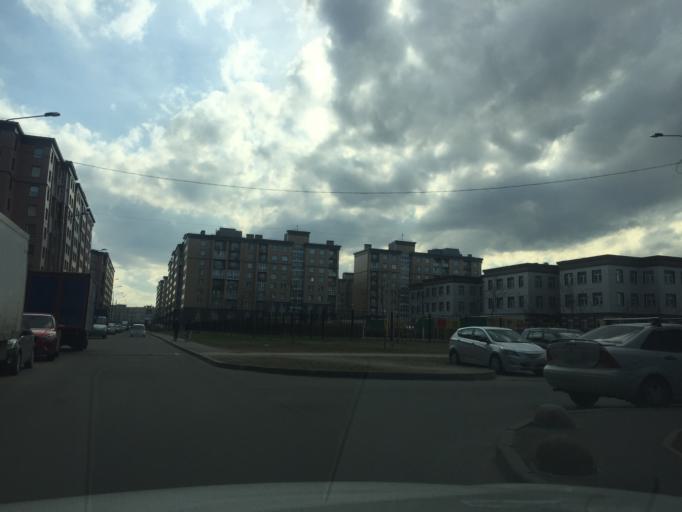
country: RU
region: St.-Petersburg
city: Tyarlevo
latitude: 59.7389
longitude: 30.4748
